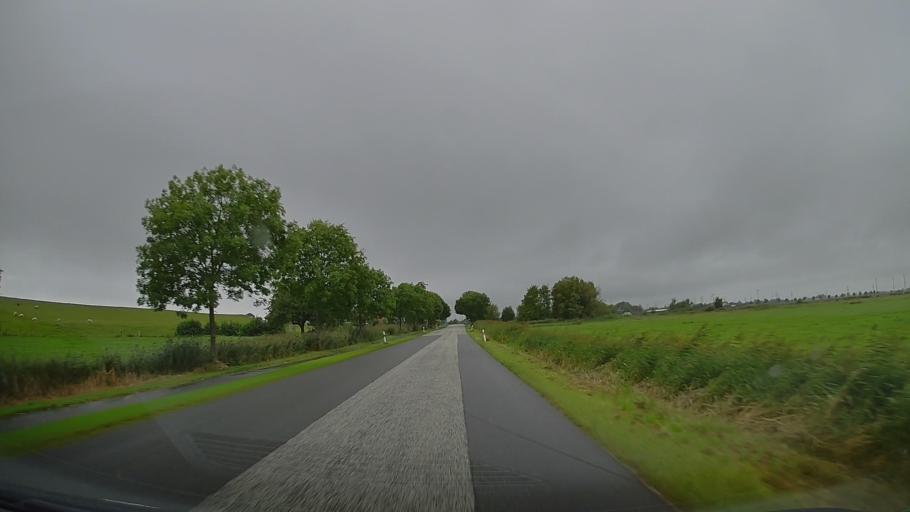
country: DE
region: Schleswig-Holstein
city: Sankt Margarethen
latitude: 53.8777
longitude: 9.2791
